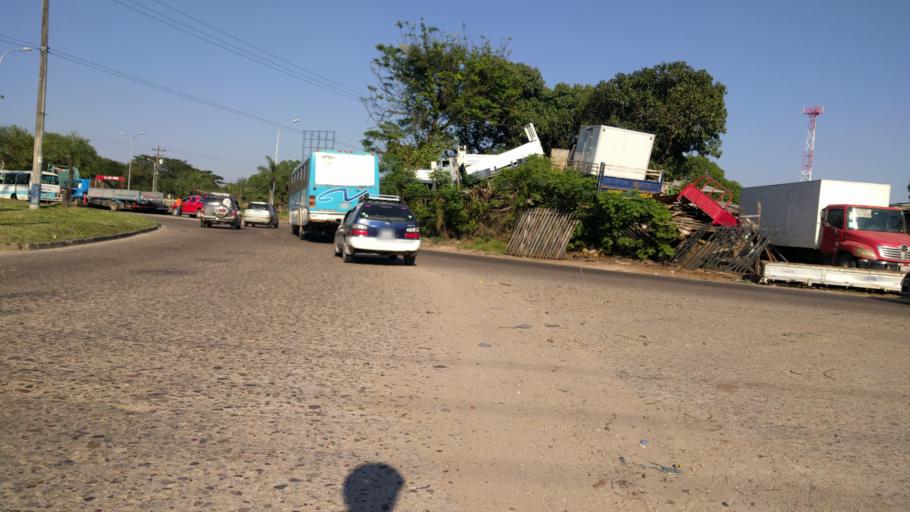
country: BO
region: Santa Cruz
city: Santa Cruz de la Sierra
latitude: -17.8217
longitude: -63.1891
